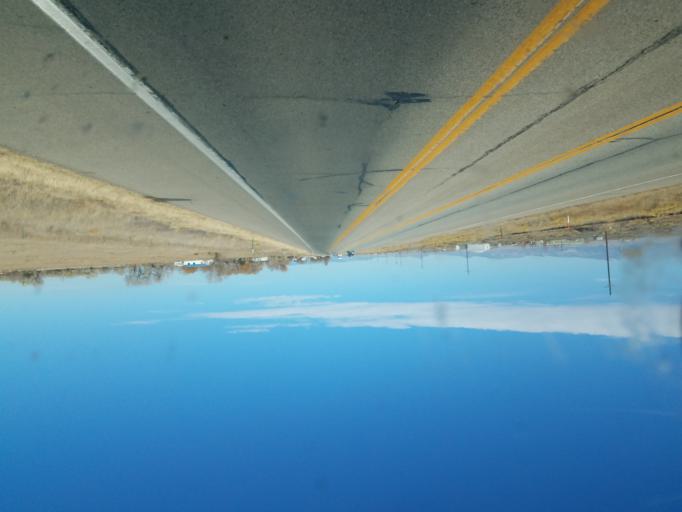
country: US
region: Colorado
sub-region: Alamosa County
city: Alamosa
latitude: 37.5038
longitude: -105.9619
